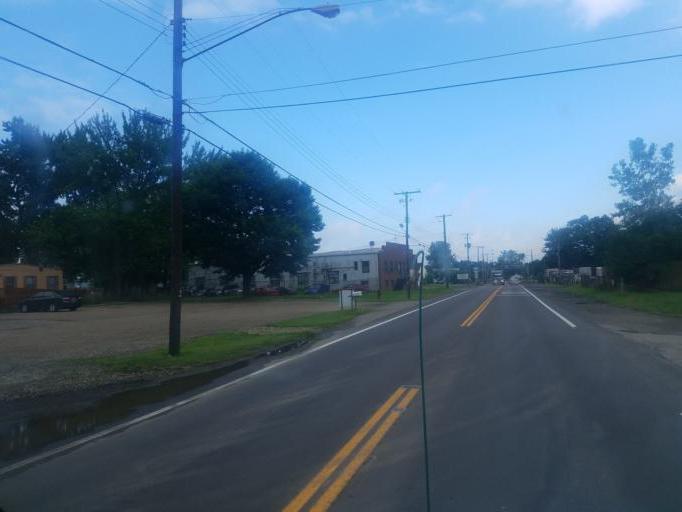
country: US
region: Ohio
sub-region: Stark County
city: Canton
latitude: 40.7812
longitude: -81.3470
